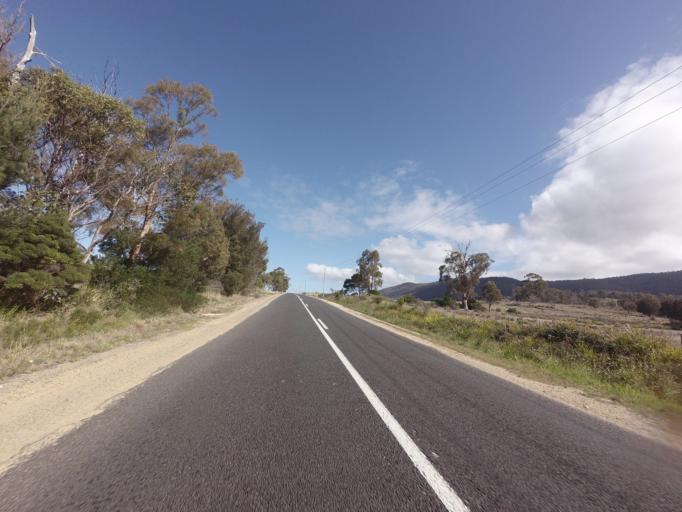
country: AU
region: Tasmania
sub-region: Break O'Day
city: St Helens
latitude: -41.7068
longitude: 148.2747
